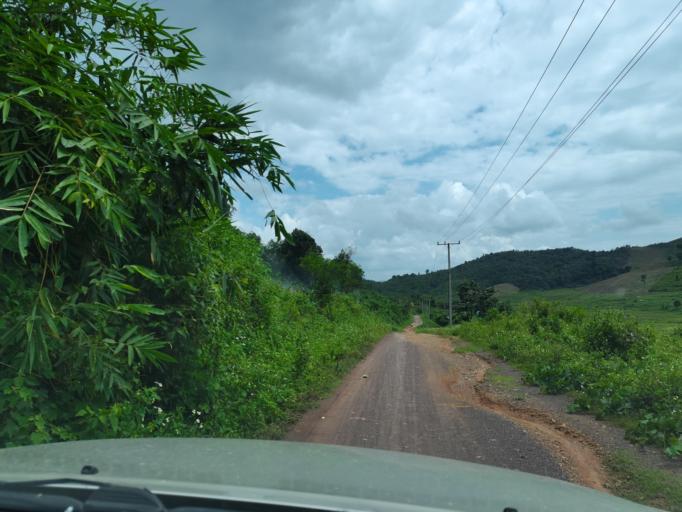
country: LA
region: Loungnamtha
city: Muang Long
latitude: 20.7096
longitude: 101.0110
